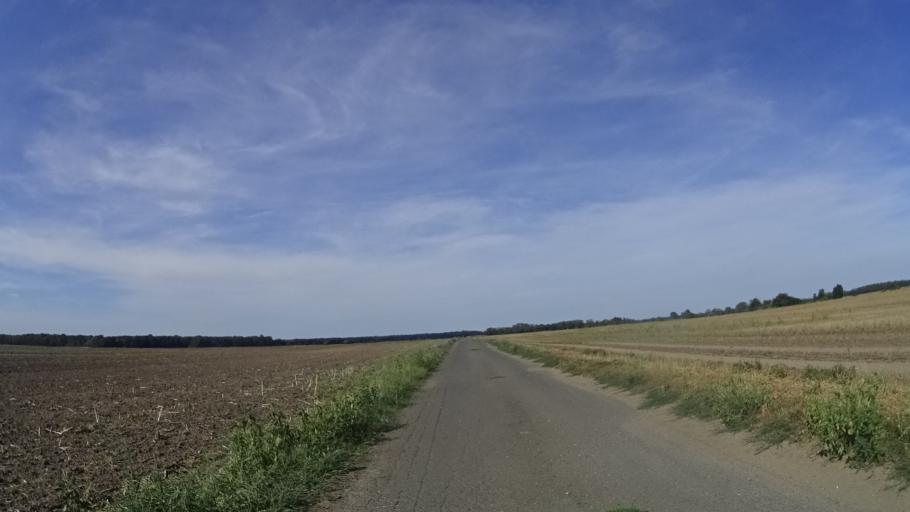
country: AT
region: Lower Austria
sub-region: Politischer Bezirk Ganserndorf
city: Durnkrut
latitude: 48.4379
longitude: 16.8741
